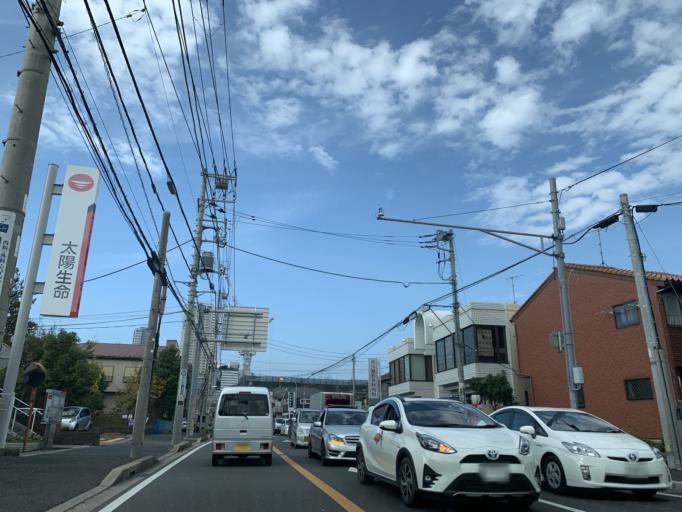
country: JP
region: Chiba
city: Funabashi
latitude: 35.7202
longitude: 139.9342
